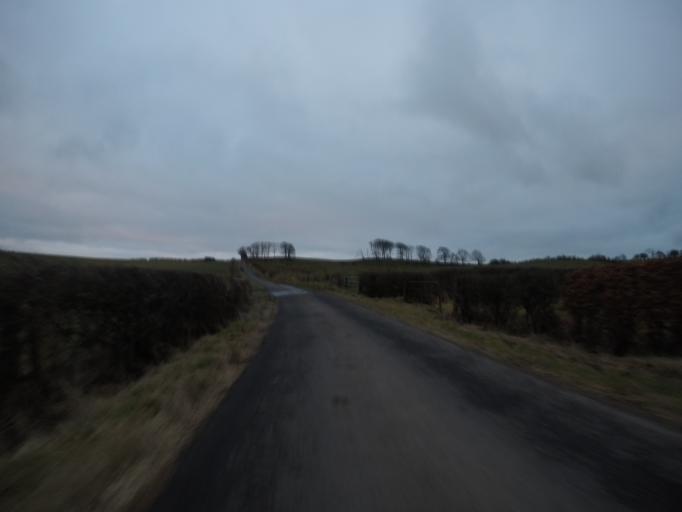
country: GB
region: Scotland
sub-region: North Ayrshire
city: Dalry
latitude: 55.6866
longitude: -4.7362
